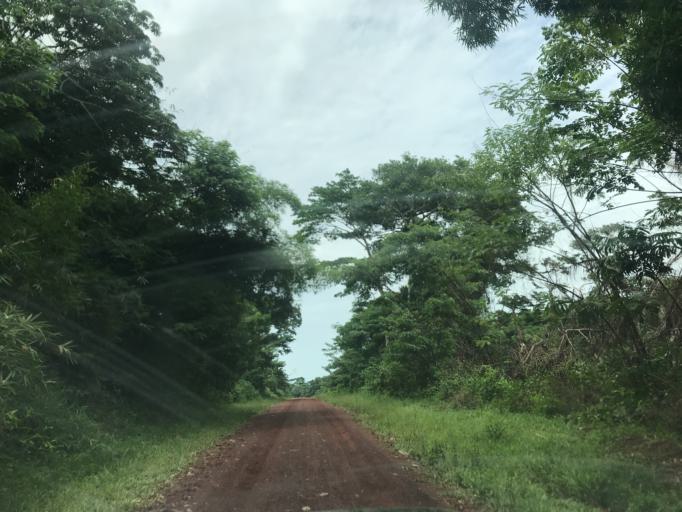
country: CD
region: Eastern Province
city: Buta
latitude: 2.3824
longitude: 24.9205
